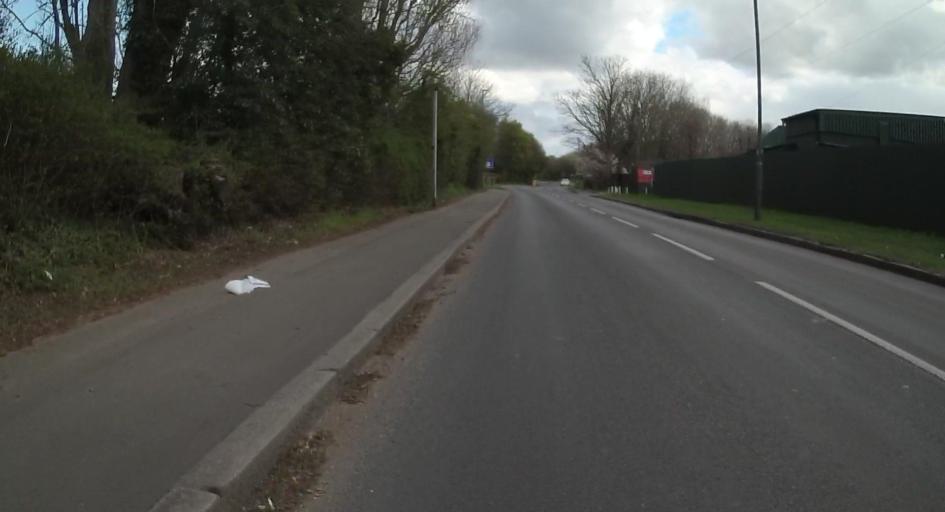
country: GB
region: England
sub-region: Surrey
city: Shepperton
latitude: 51.3900
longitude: -0.4670
